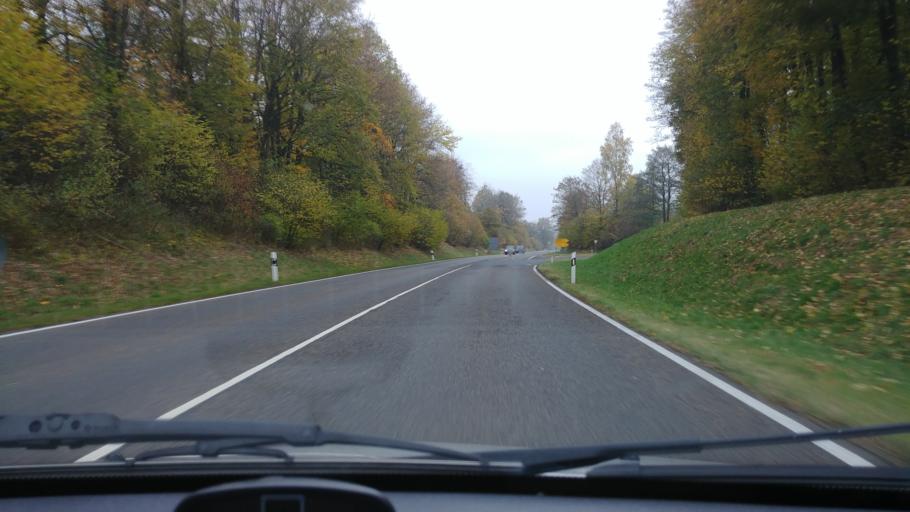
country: DE
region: Rheinland-Pfalz
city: Rotenhain
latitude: 50.6016
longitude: 7.8903
